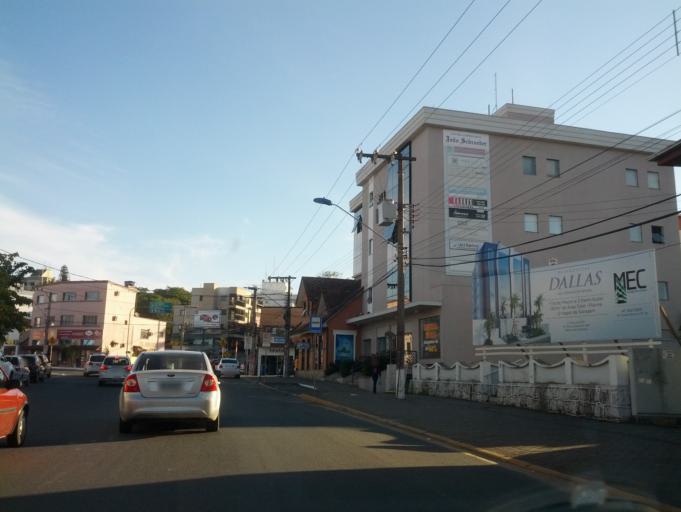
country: BR
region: Santa Catarina
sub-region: Indaial
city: Indaial
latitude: -26.8945
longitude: -49.2337
